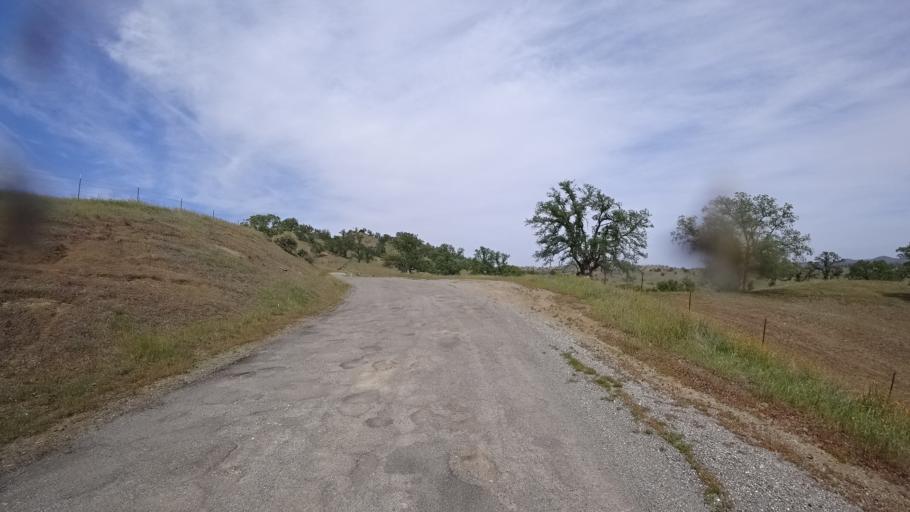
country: US
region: California
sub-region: Glenn County
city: Willows
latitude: 39.6115
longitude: -122.5823
